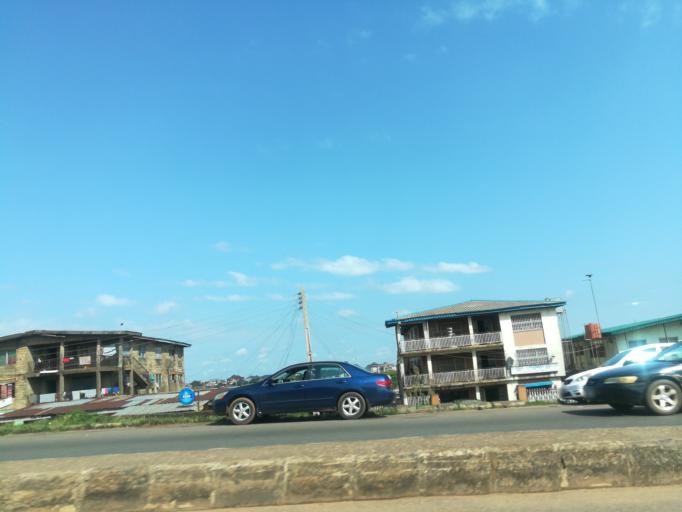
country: NG
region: Oyo
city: Ibadan
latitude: 7.4137
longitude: 3.9565
